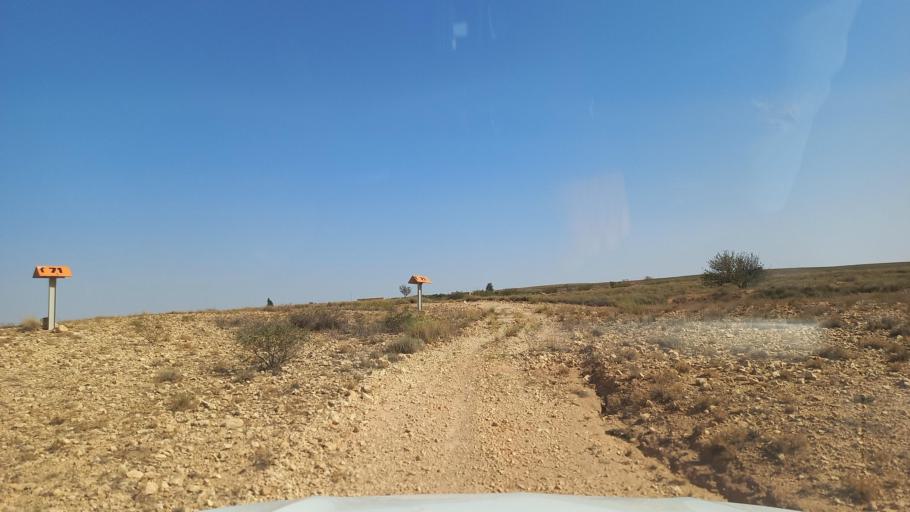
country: TN
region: Al Qasrayn
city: Kasserine
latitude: 35.2144
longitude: 8.9837
